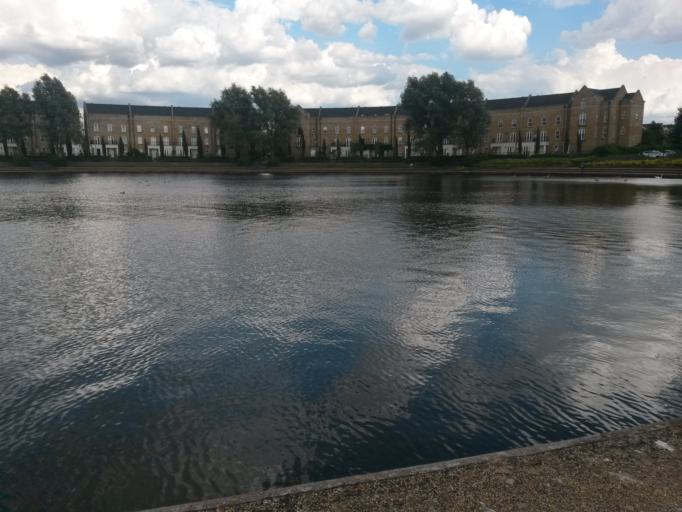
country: GB
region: England
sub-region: Milton Keynes
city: Simpson
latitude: 52.0075
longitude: -0.7022
